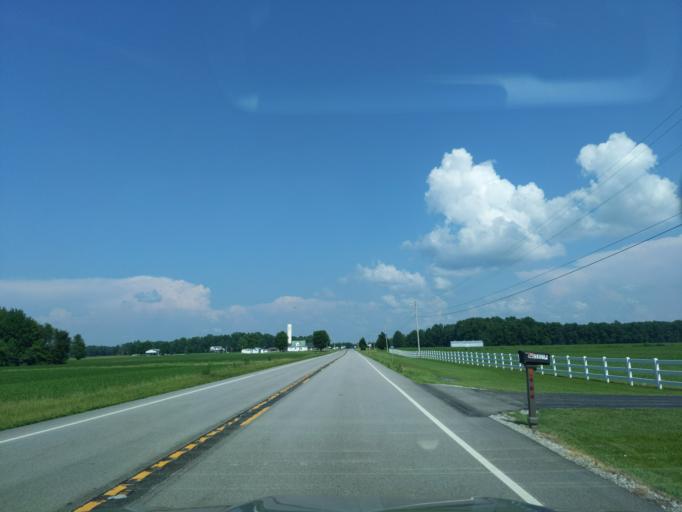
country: US
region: Indiana
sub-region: Ripley County
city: Osgood
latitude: 39.0750
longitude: -85.3560
